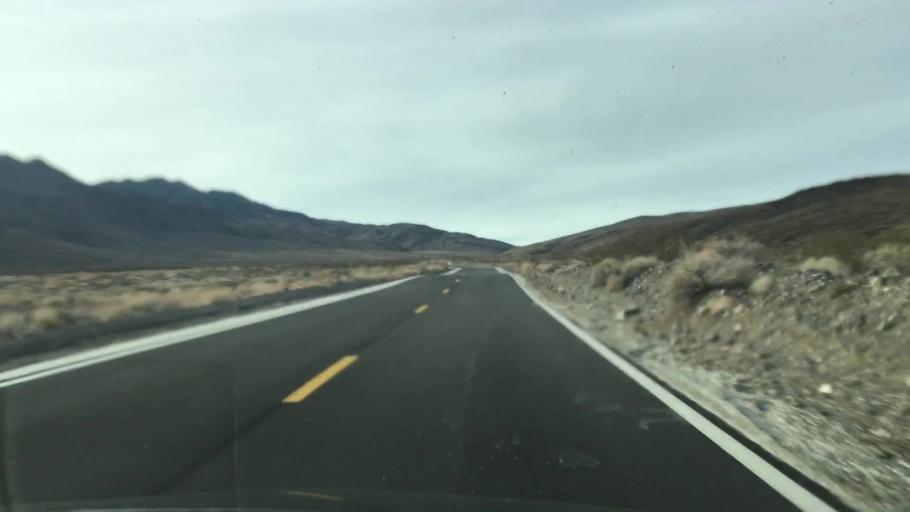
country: US
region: Nevada
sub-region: Nye County
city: Beatty
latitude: 36.4580
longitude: -117.2389
